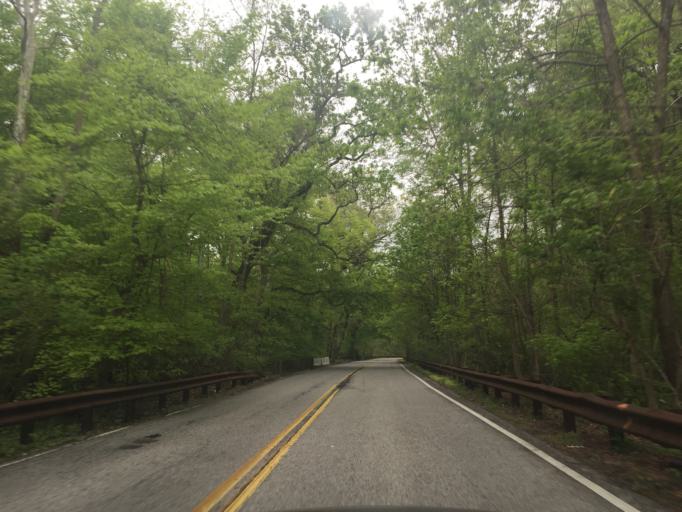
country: US
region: Maryland
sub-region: Baltimore County
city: Charlestown
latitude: 39.3006
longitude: -76.7032
